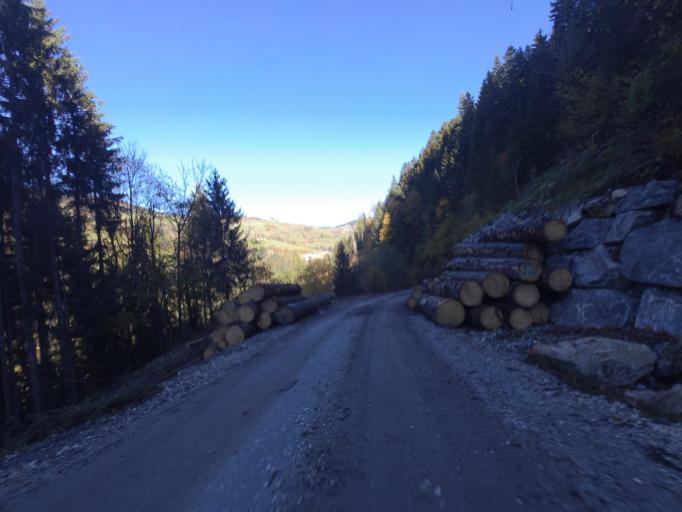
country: AT
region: Salzburg
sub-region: Politischer Bezirk Sankt Johann im Pongau
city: Sankt Johann im Pongau
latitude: 47.3280
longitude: 13.2370
